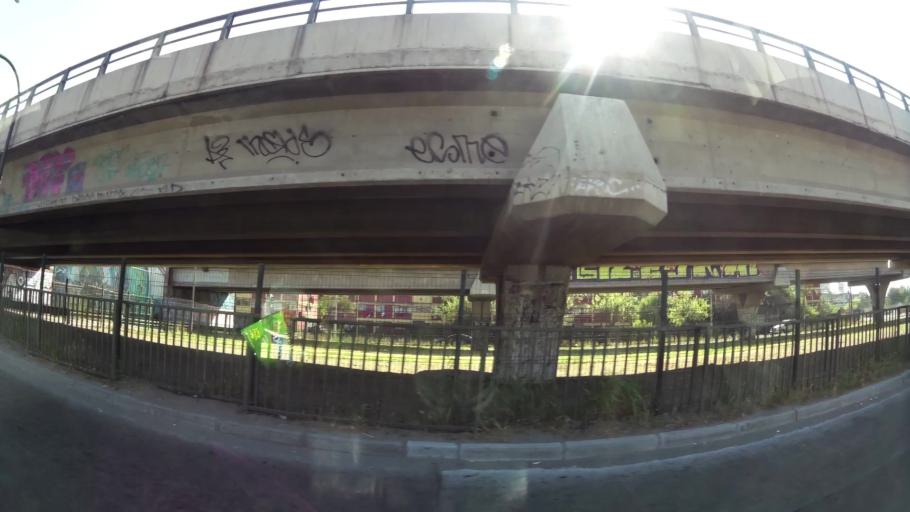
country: CL
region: Santiago Metropolitan
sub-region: Provincia de Santiago
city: Villa Presidente Frei, Nunoa, Santiago, Chile
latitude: -33.4710
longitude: -70.5766
